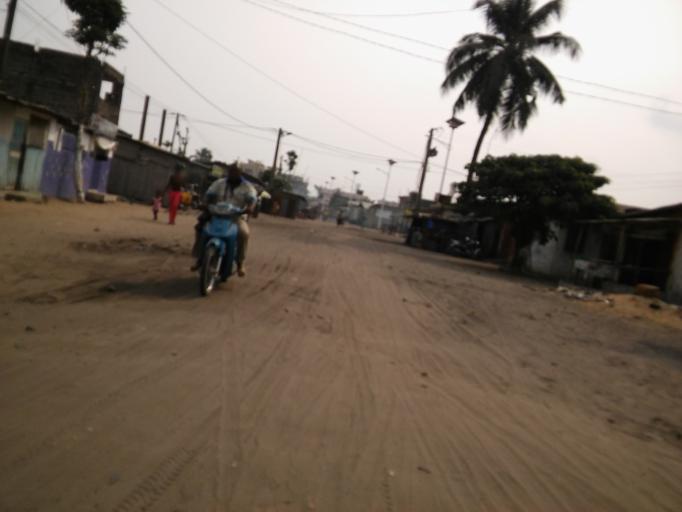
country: BJ
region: Littoral
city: Cotonou
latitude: 6.3931
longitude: 2.3786
